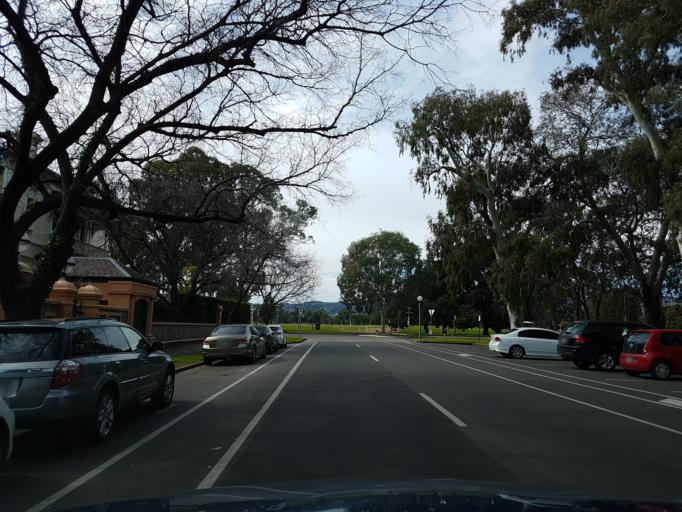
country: AU
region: South Australia
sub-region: Adelaide
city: Adelaide
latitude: -34.9349
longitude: 138.6170
